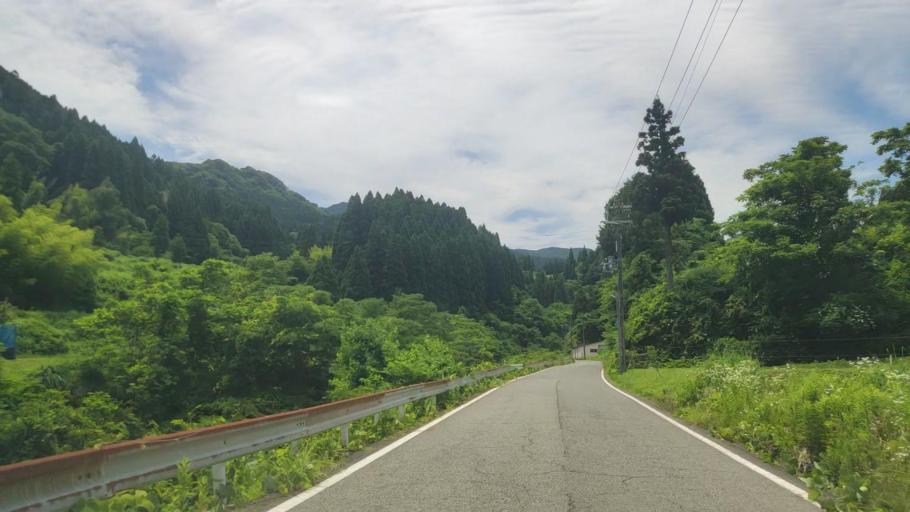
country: JP
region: Tottori
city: Tottori
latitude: 35.4268
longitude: 134.5280
